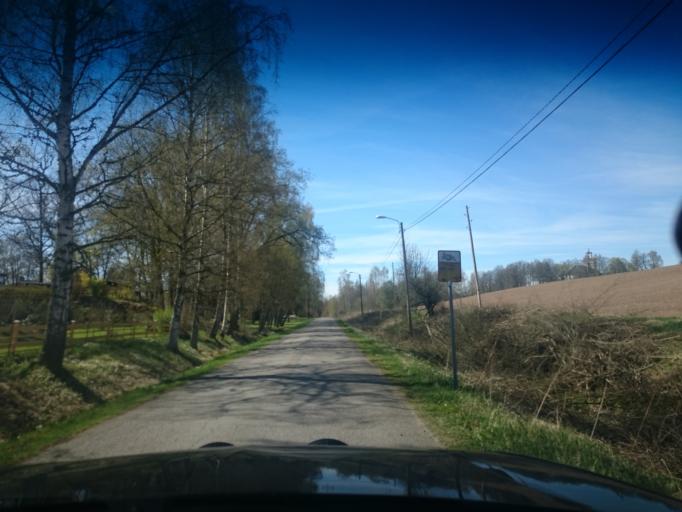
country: SE
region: Kronoberg
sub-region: Uppvidinge Kommun
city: Aseda
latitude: 57.3709
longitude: 15.3776
